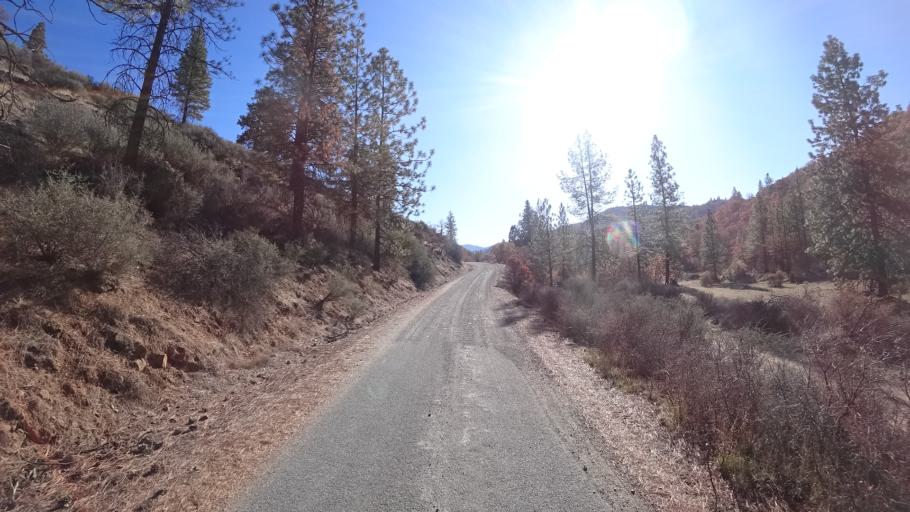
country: US
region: California
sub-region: Siskiyou County
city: Yreka
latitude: 41.8341
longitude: -122.8374
